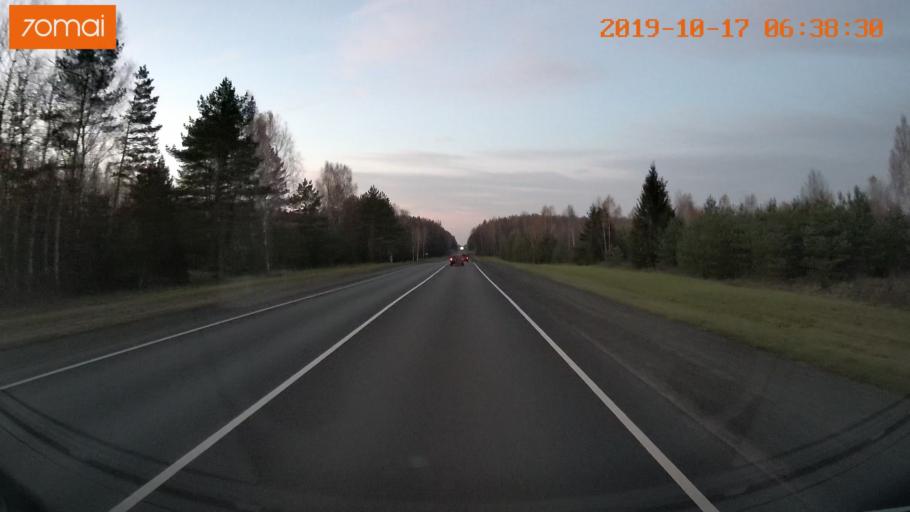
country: RU
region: Ivanovo
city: Novoye Leushino
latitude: 56.6550
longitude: 40.5868
